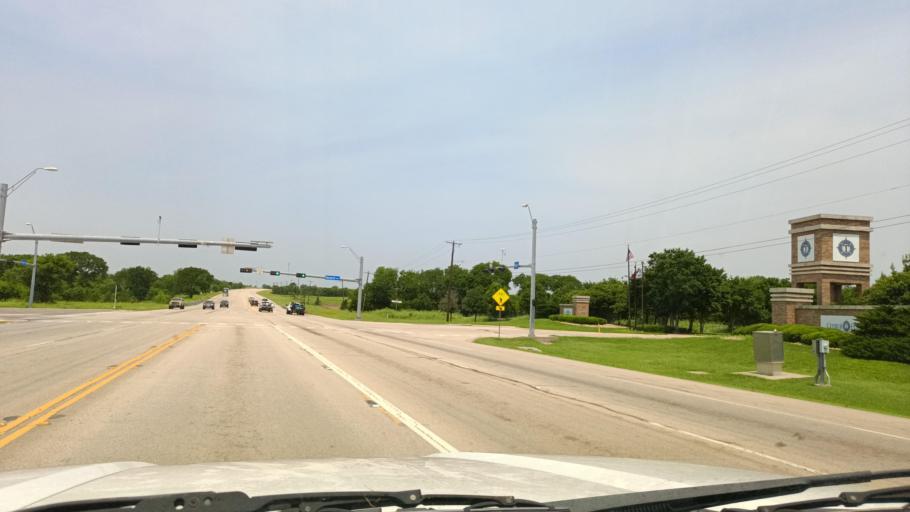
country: US
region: Texas
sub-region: Bell County
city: Temple
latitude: 31.1289
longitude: -97.3990
